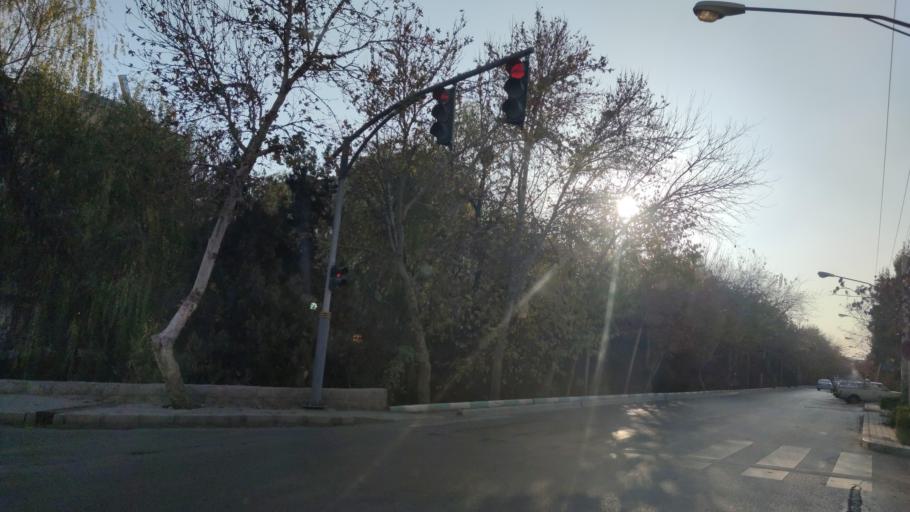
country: IR
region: Isfahan
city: Isfahan
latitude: 32.7095
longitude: 51.6858
